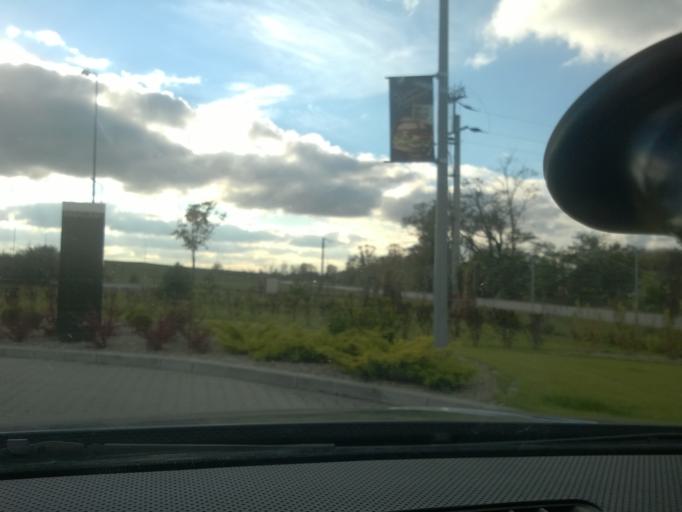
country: PL
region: Masovian Voivodeship
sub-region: Powiat pruszkowski
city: Brwinow
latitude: 52.1564
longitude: 20.6847
